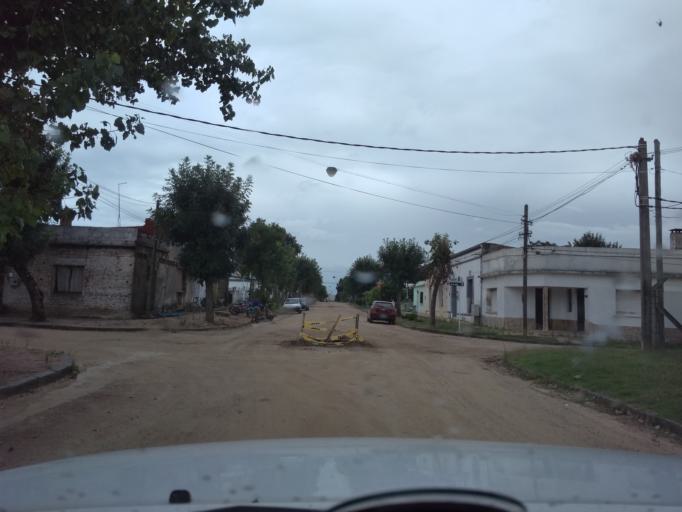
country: UY
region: Canelones
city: Tala
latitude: -34.1965
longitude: -55.7388
